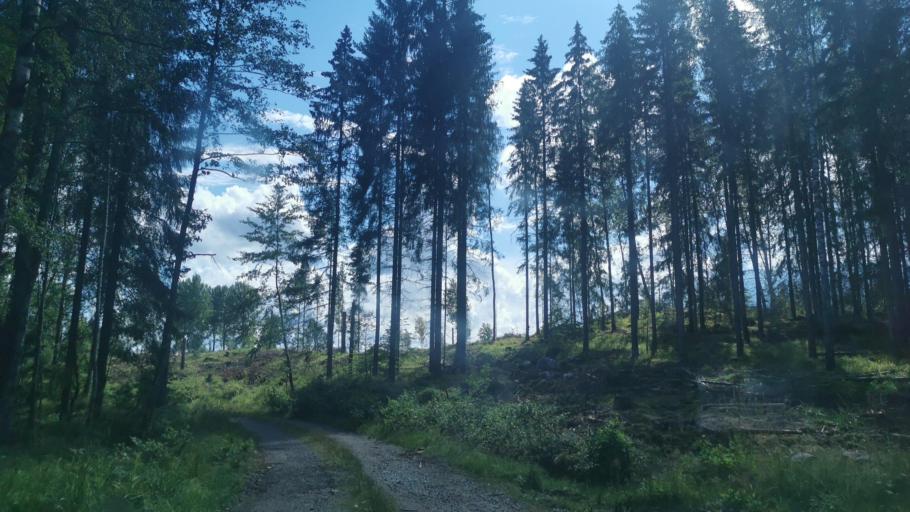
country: SE
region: OEstergoetland
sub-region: Finspangs Kommun
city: Finspang
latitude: 58.8001
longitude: 15.8042
